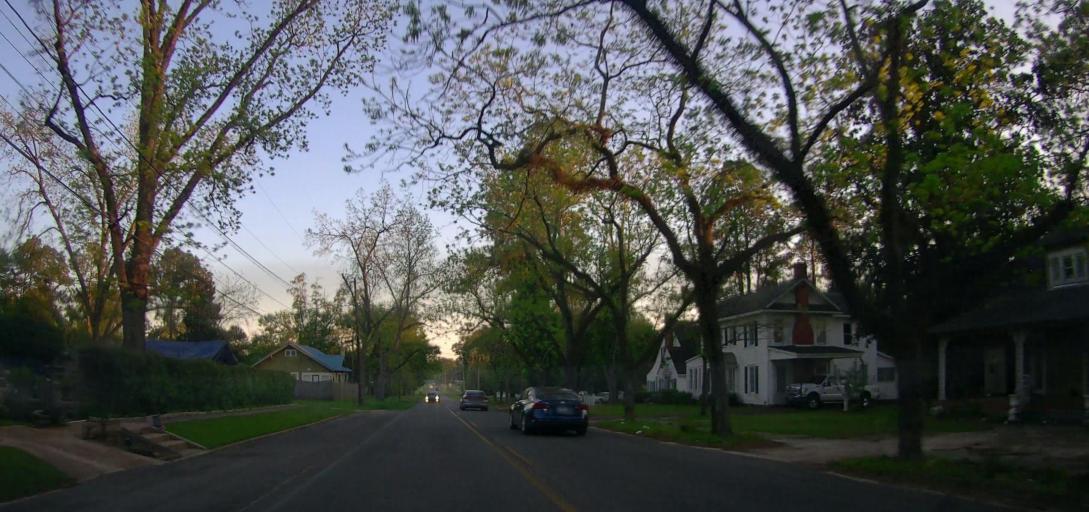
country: US
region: Georgia
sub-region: Ben Hill County
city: Fitzgerald
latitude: 31.7133
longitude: -83.2649
